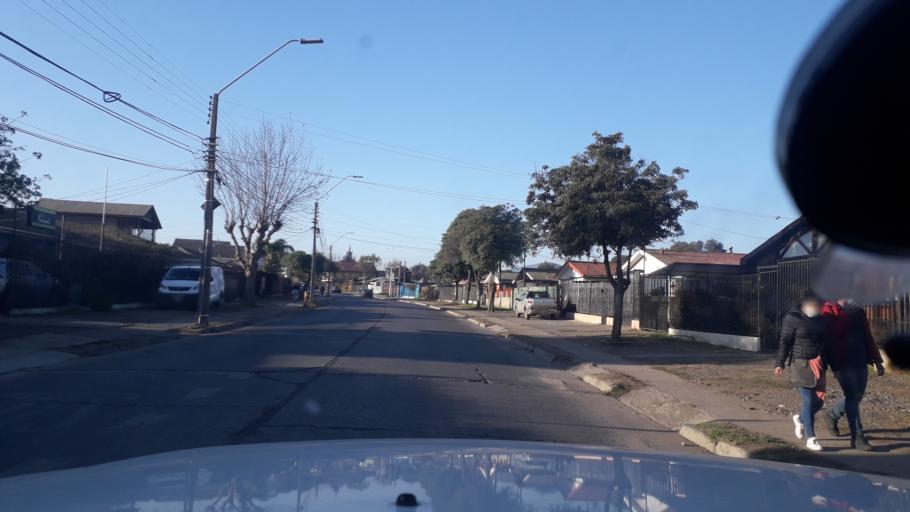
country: CL
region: Valparaiso
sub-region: Provincia de Valparaiso
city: Vina del Mar
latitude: -32.9293
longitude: -71.5185
